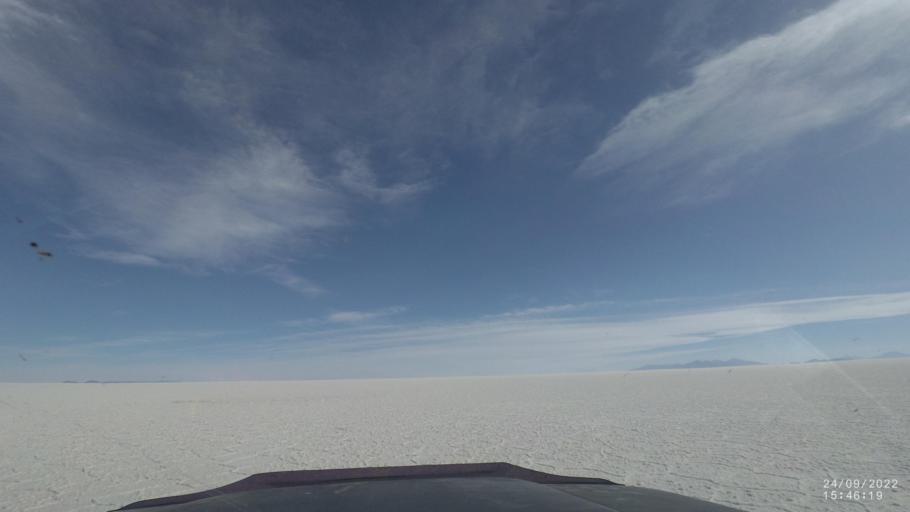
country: BO
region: Potosi
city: Colchani
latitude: -20.2662
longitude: -67.2223
